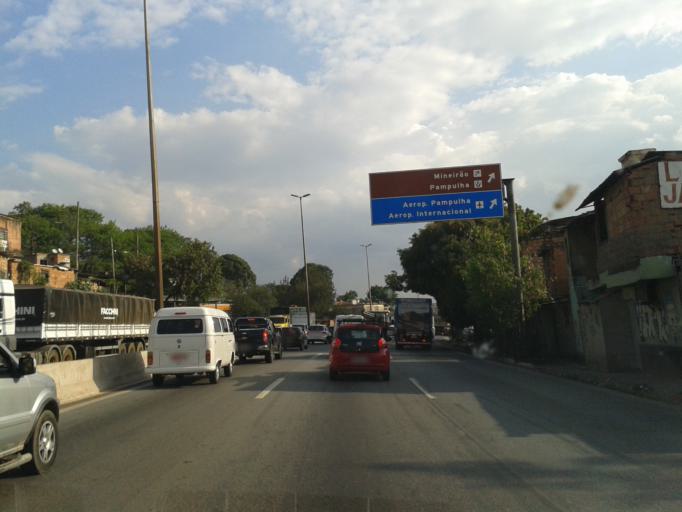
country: BR
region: Minas Gerais
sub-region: Belo Horizonte
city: Belo Horizonte
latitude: -19.8748
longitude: -43.9498
